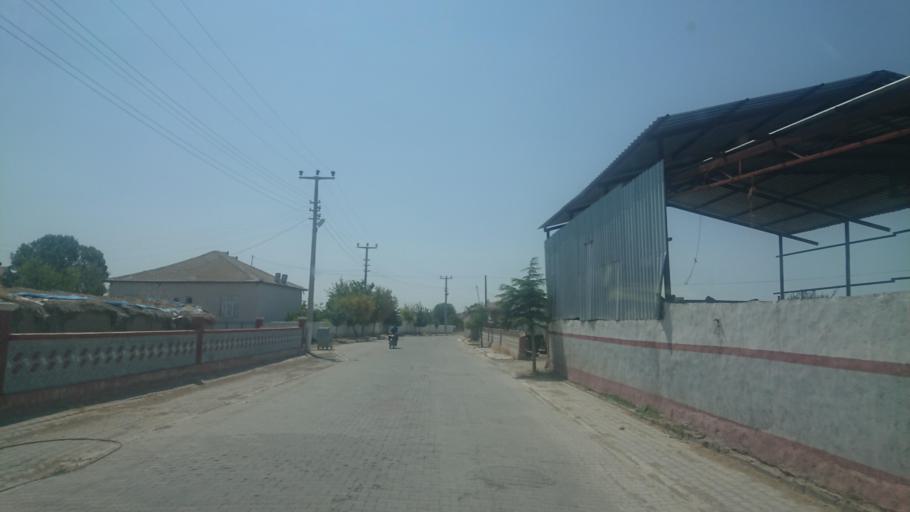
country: TR
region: Aksaray
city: Yesilova
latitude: 38.3455
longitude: 33.7509
